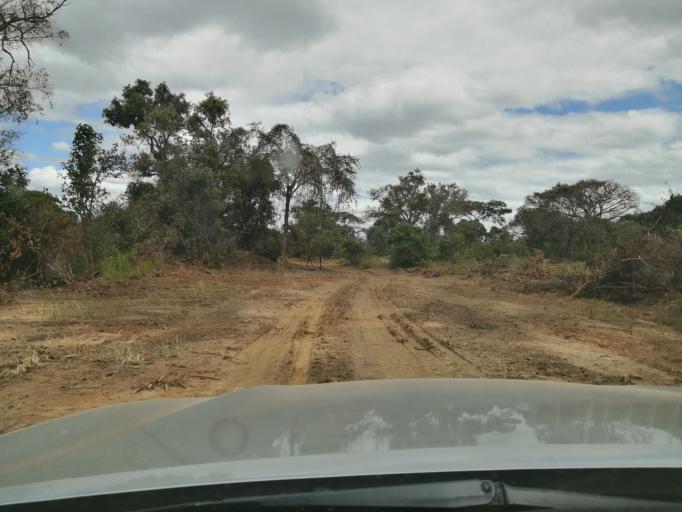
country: ZM
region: Central
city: Mumbwa
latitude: -14.5853
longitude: 27.1958
